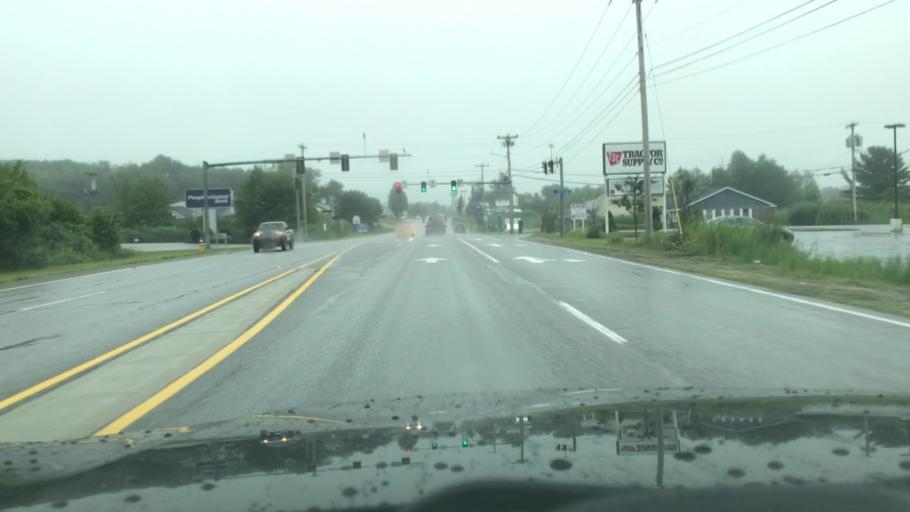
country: US
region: Maine
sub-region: Cumberland County
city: West Scarborough
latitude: 43.5814
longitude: -70.3669
